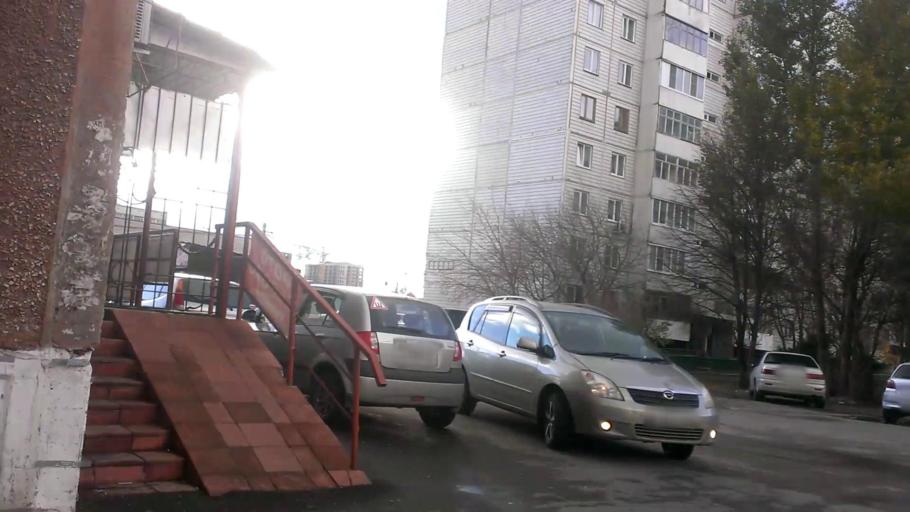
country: RU
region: Altai Krai
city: Novosilikatnyy
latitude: 53.3565
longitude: 83.6764
